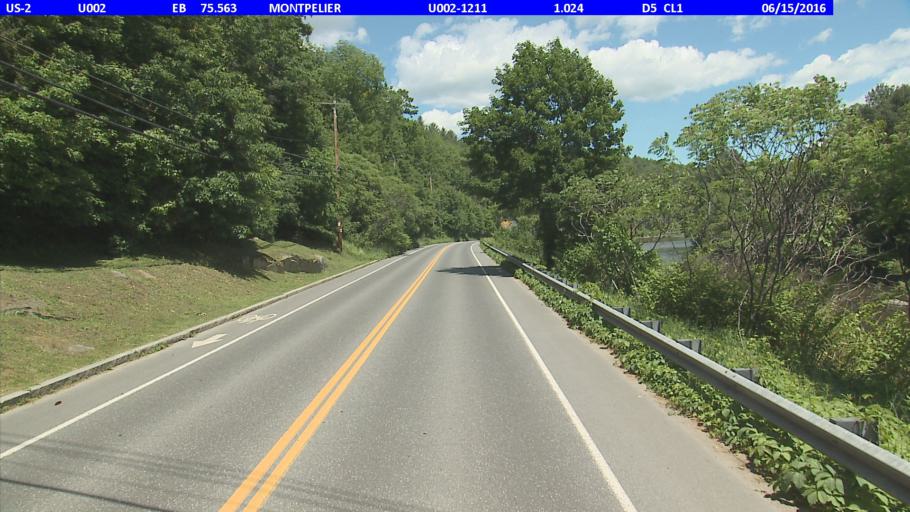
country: US
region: Vermont
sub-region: Washington County
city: Montpelier
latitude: 44.2576
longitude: -72.5931
